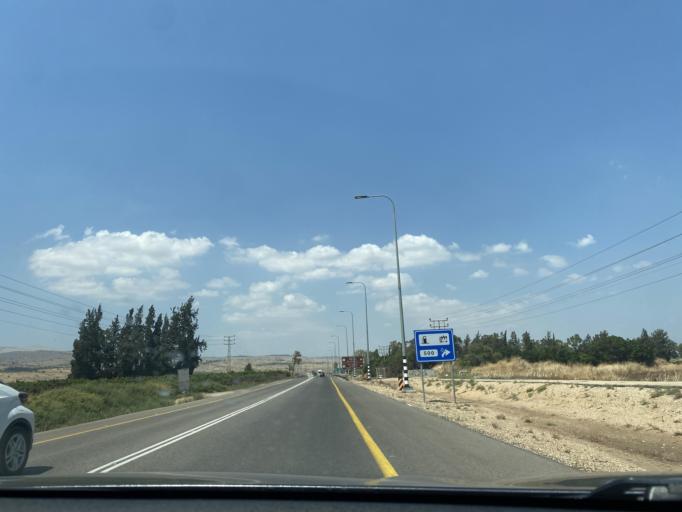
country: IL
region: Northern District
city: Tiberias
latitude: 32.8414
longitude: 35.5134
